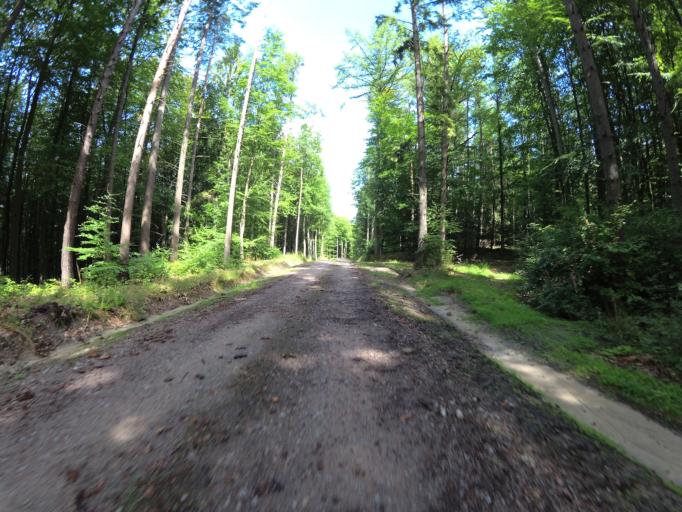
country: PL
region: Pomeranian Voivodeship
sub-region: Powiat wejherowski
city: Bojano
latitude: 54.5133
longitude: 18.4228
